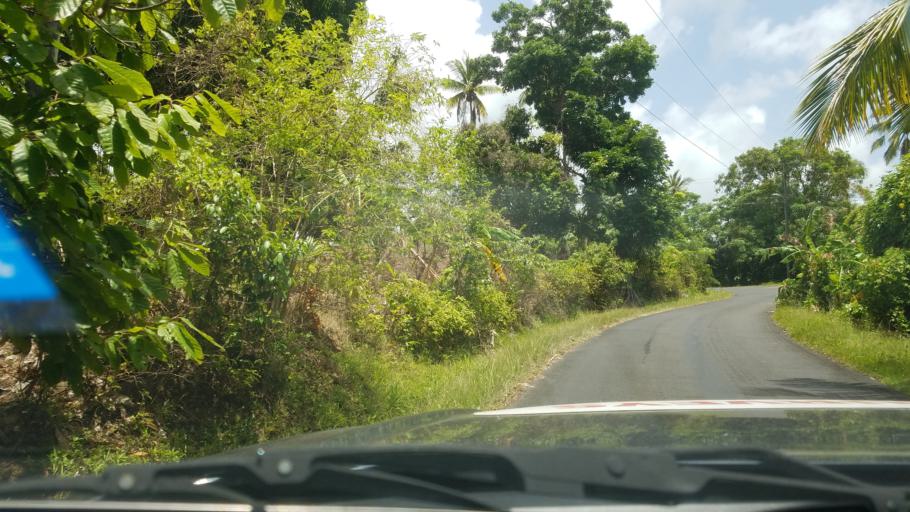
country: LC
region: Castries Quarter
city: Bisee
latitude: 14.0006
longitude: -60.9169
